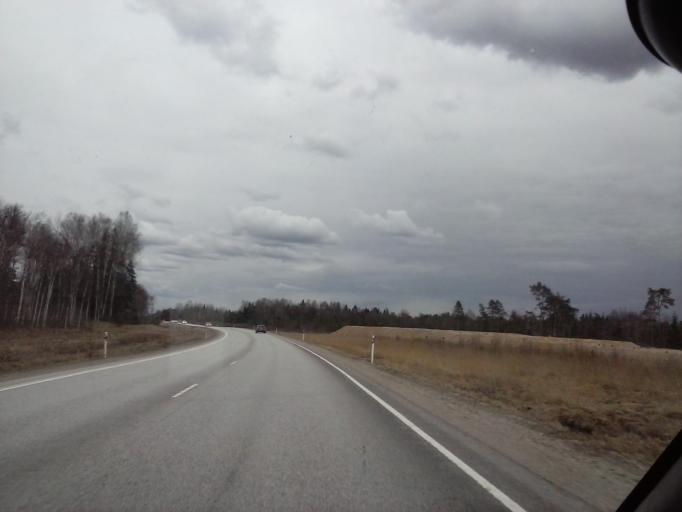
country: EE
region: Jaervamaa
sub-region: Paide linn
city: Paide
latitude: 59.0346
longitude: 25.4556
